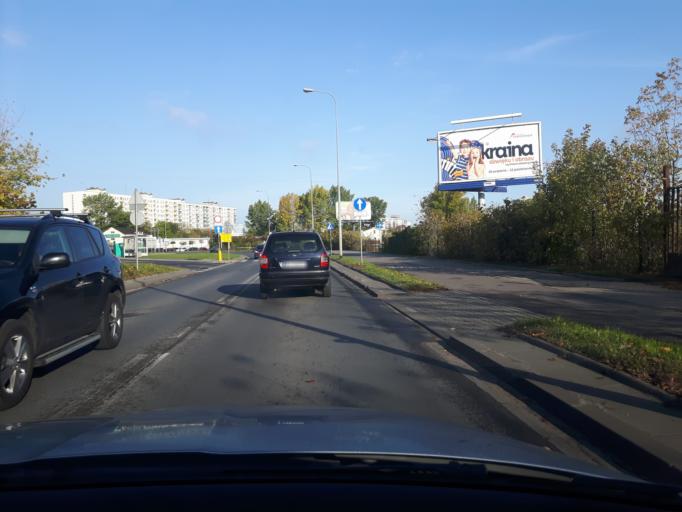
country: PL
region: Masovian Voivodeship
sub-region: Warszawa
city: Targowek
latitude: 52.2854
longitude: 21.0506
